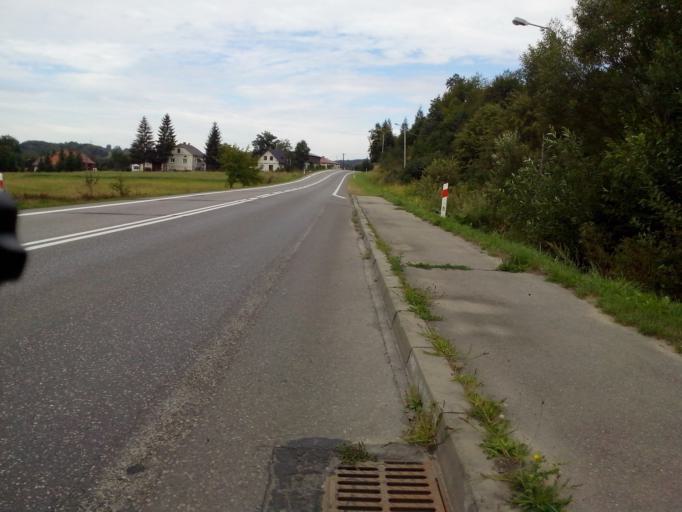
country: PL
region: Subcarpathian Voivodeship
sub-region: Powiat brzozowski
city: Blizne
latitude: 49.7658
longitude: 21.9594
